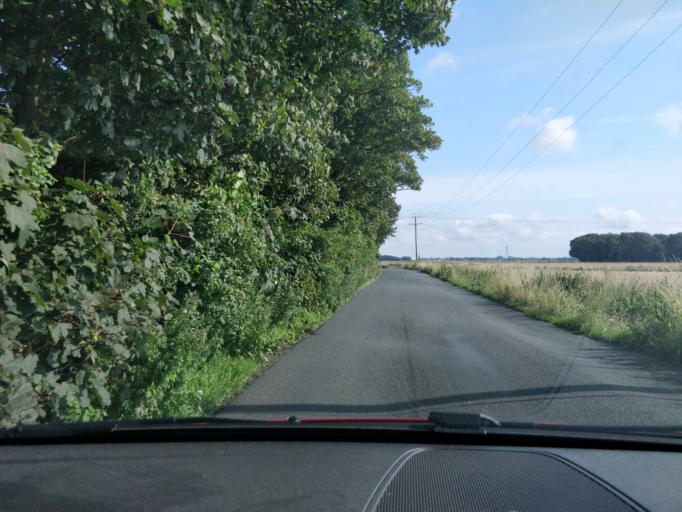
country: GB
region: England
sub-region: Lancashire
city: Banks
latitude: 53.6517
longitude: -2.9489
